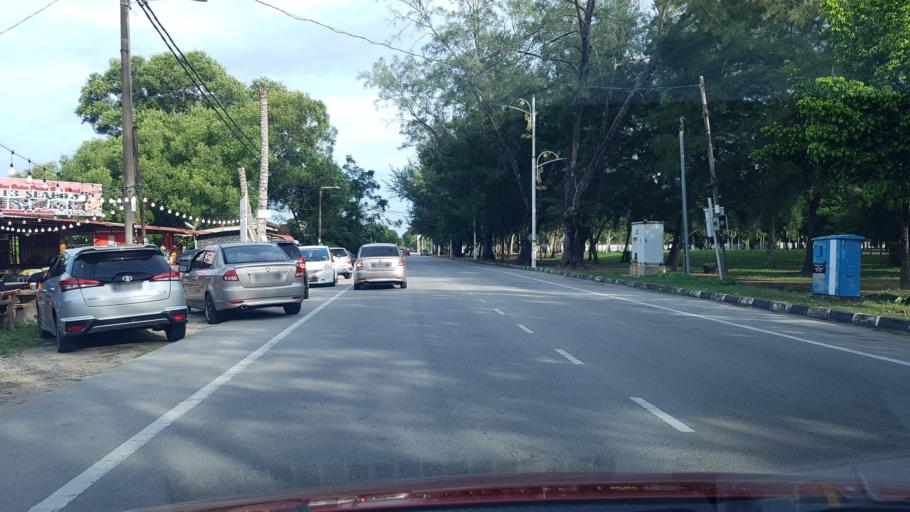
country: MY
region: Terengganu
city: Kuala Terengganu
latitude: 5.3196
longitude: 103.1556
